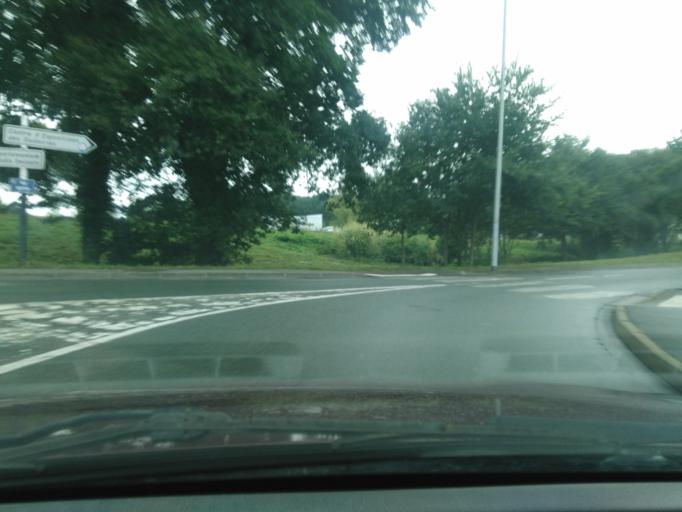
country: FR
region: Pays de la Loire
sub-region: Departement de la Vendee
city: La Roche-sur-Yon
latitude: 46.6735
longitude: -1.4038
